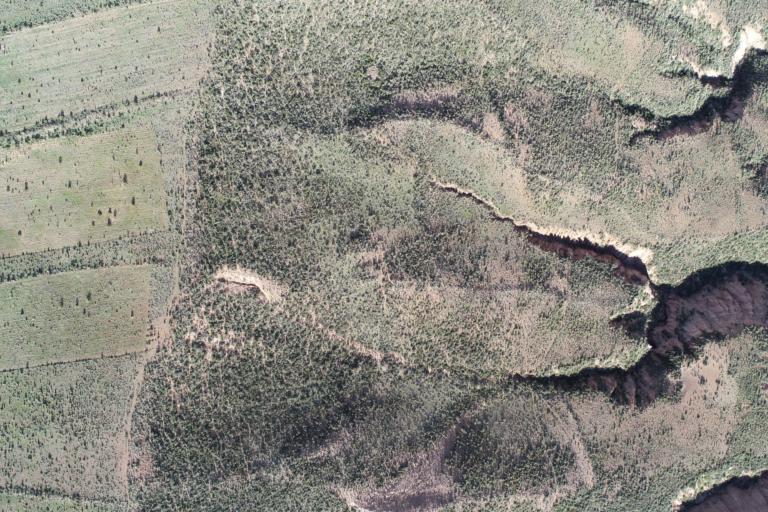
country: BO
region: La Paz
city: Curahuara de Carangas
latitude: -17.3005
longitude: -68.4933
